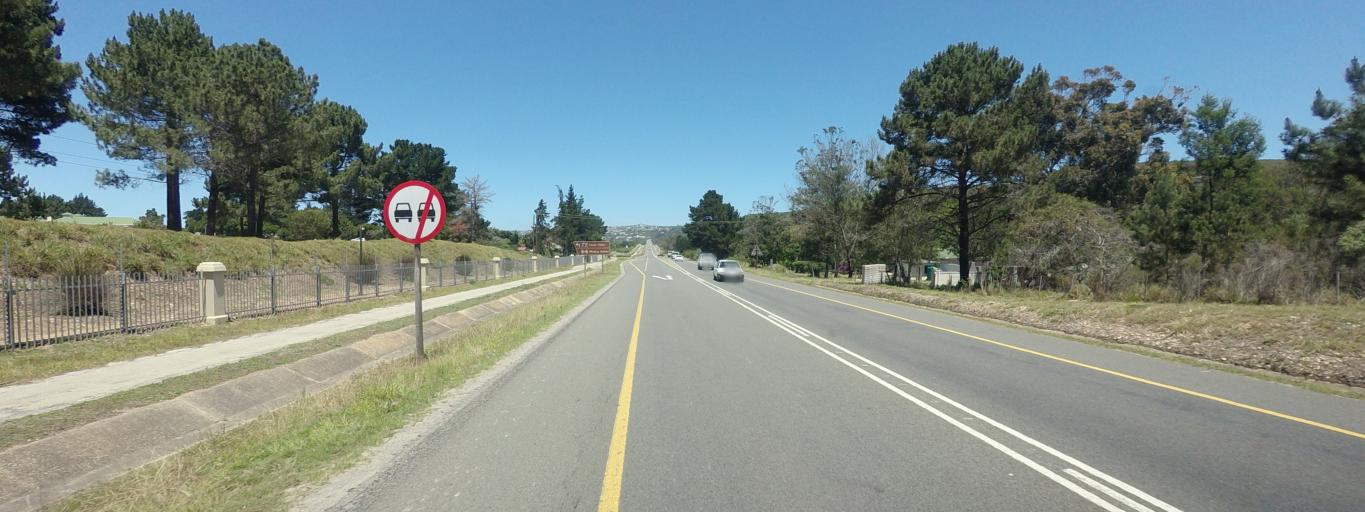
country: ZA
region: Western Cape
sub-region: Eden District Municipality
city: Plettenberg Bay
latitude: -34.0245
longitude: 23.3803
